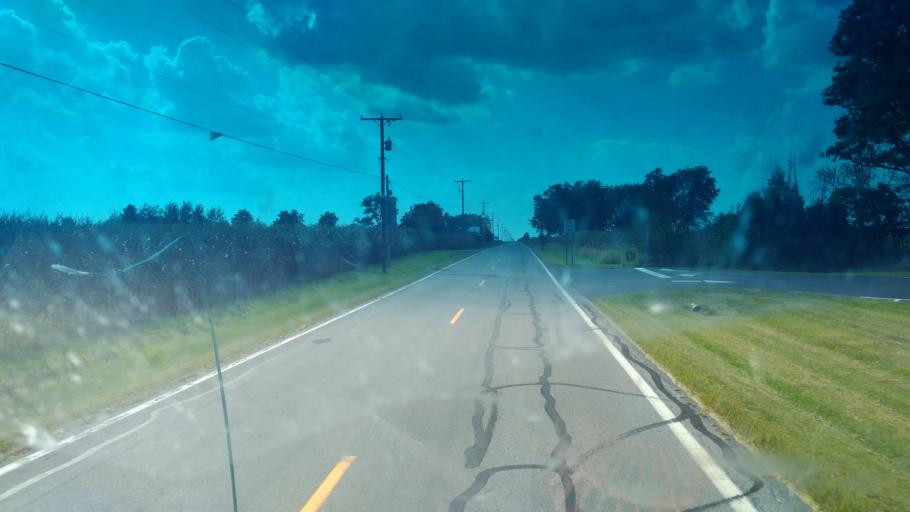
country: US
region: Ohio
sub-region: Hancock County
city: Arlington
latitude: 40.7795
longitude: -83.6616
